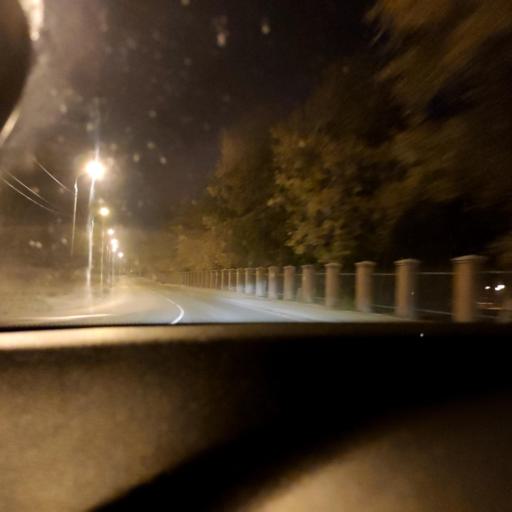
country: RU
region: Samara
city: Petra-Dubrava
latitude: 53.2368
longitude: 50.2651
